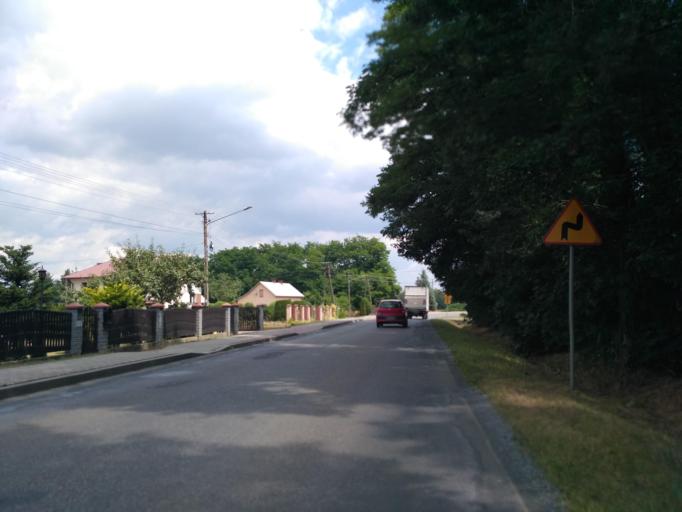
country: PL
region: Subcarpathian Voivodeship
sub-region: Powiat debicki
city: Pilzno
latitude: 50.0308
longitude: 21.3055
